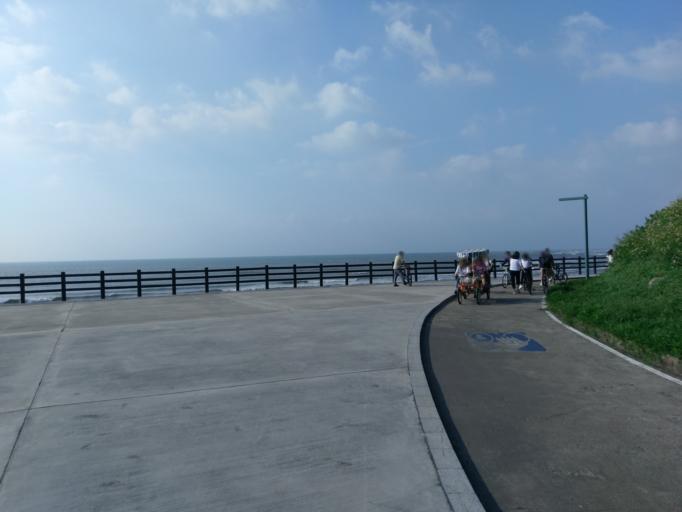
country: TW
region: Taiwan
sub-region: Hsinchu
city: Hsinchu
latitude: 24.8318
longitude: 120.9143
